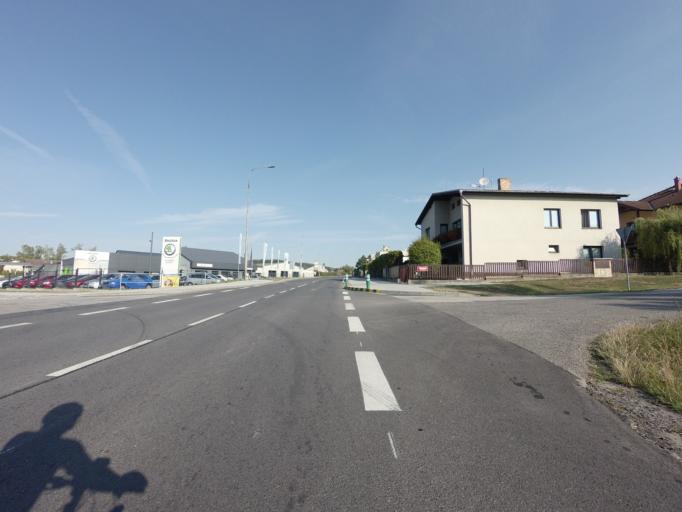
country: CZ
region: Jihocesky
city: Tyn nad Vltavou
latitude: 49.2289
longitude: 14.4229
